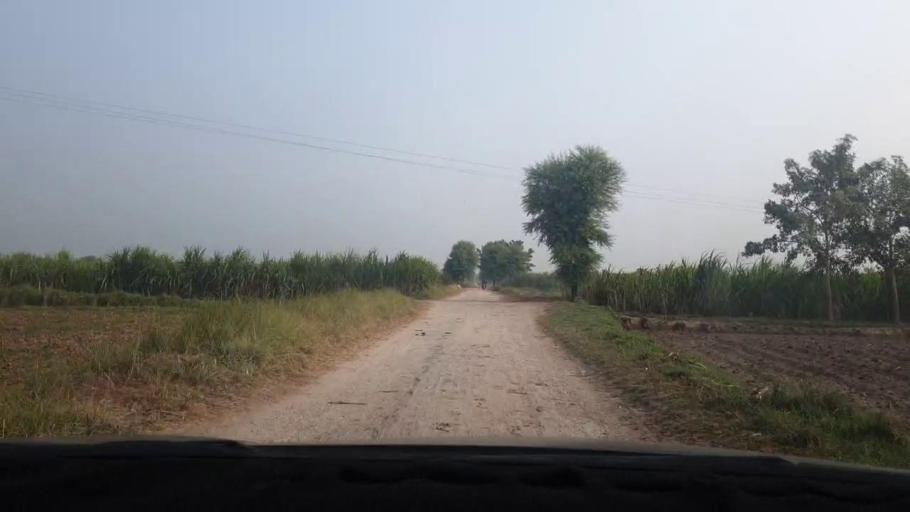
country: PK
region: Sindh
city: Matiari
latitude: 25.5762
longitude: 68.5126
